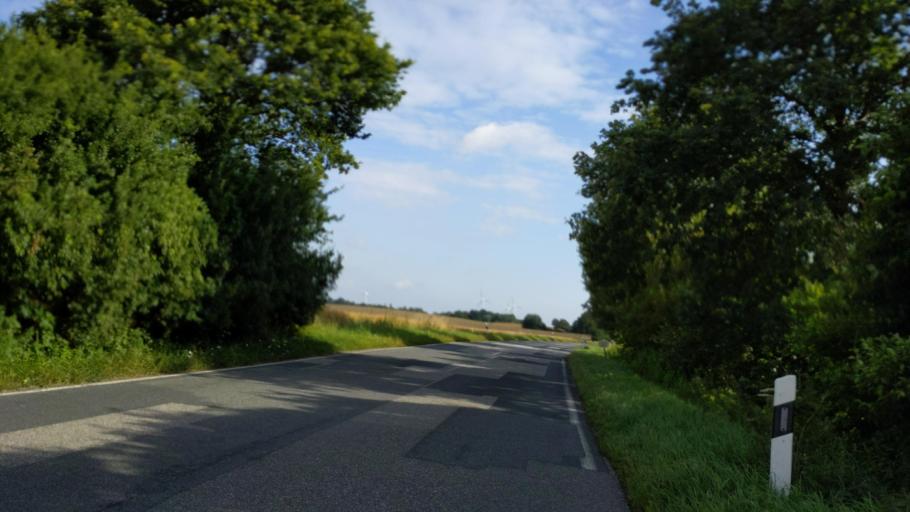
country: DE
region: Schleswig-Holstein
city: Bad Schwartau
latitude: 53.9811
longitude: 10.6583
